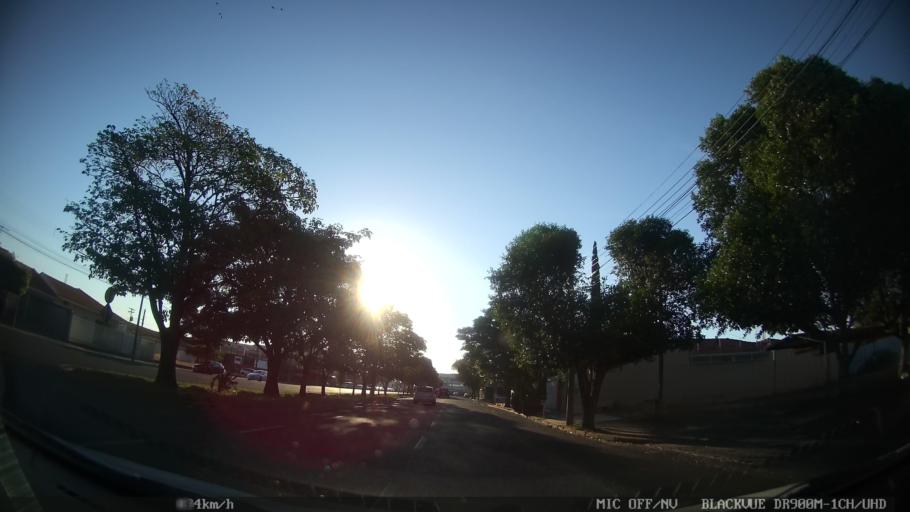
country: BR
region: Sao Paulo
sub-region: Sao Jose Do Rio Preto
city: Sao Jose do Rio Preto
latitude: -20.7927
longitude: -49.3588
